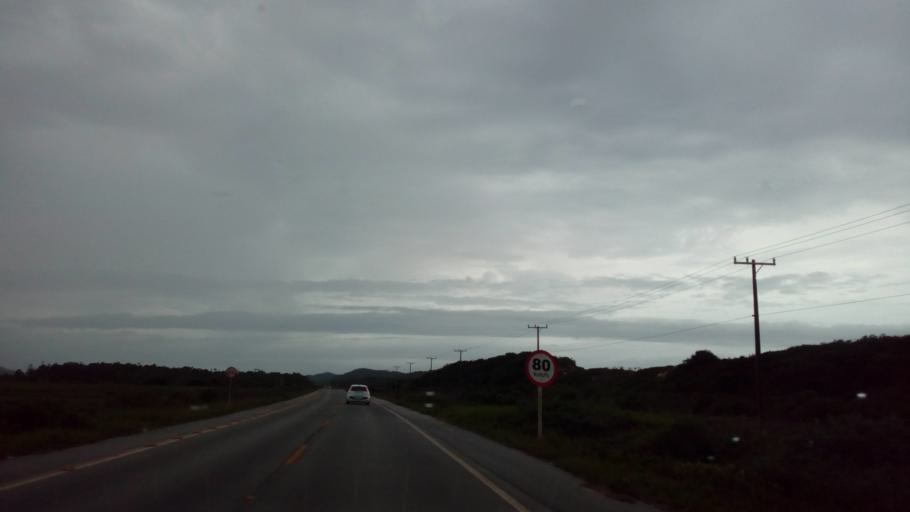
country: BR
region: Santa Catarina
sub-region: Laguna
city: Laguna
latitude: -28.5449
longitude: -48.7923
